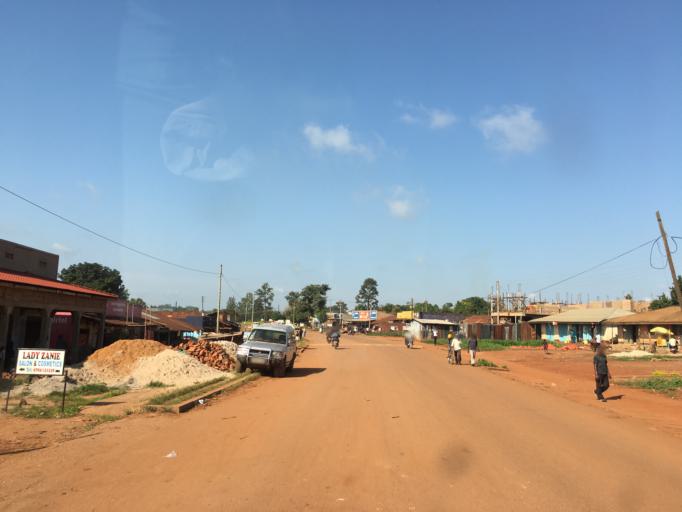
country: UG
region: Western Region
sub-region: Masindi District
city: Masindi
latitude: 1.6935
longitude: 31.7095
